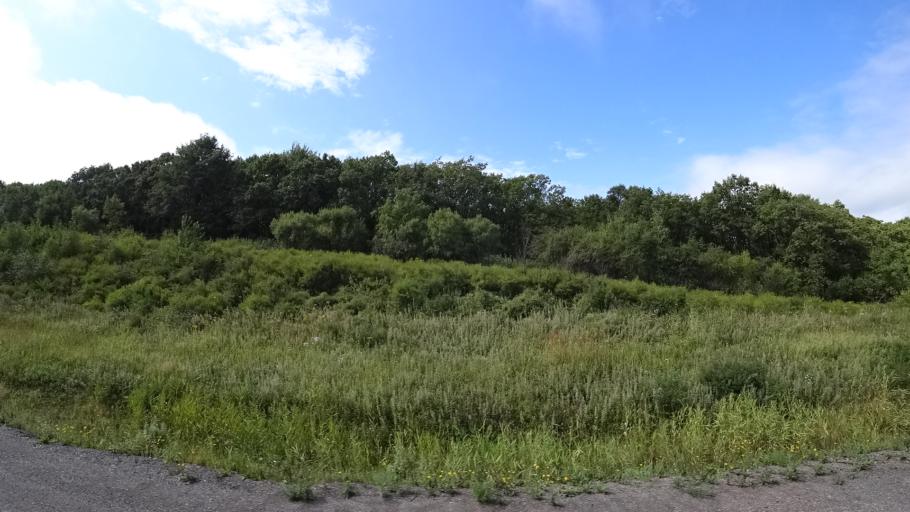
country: RU
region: Primorskiy
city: Lyalichi
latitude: 44.1242
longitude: 132.4228
